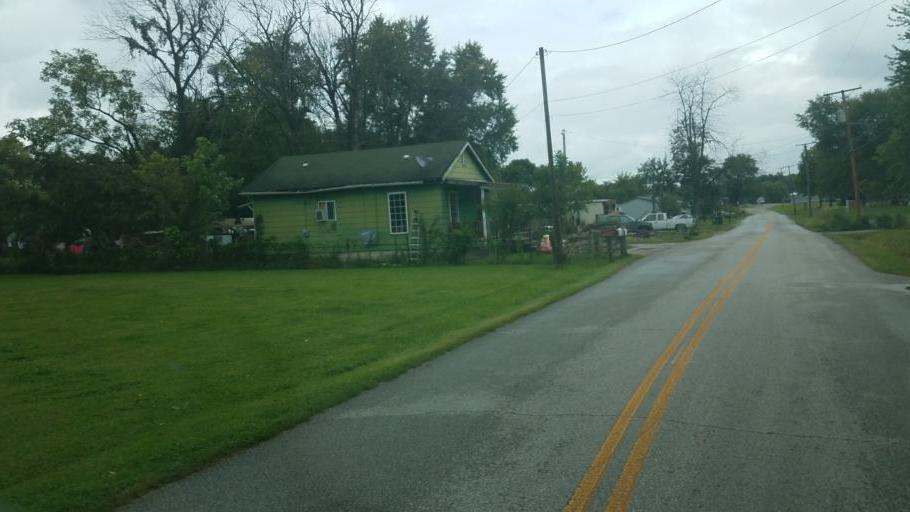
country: US
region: Ohio
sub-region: Scioto County
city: Wheelersburg
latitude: 38.7099
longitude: -82.8719
